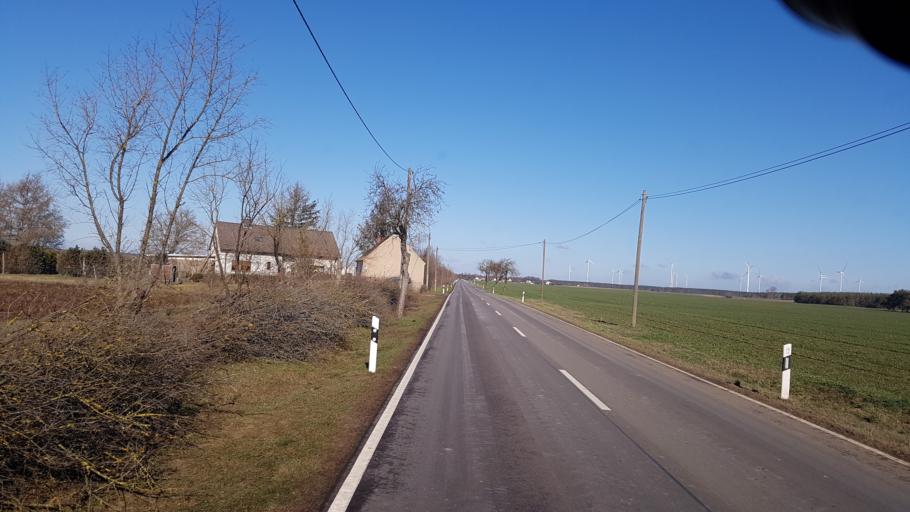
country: DE
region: Saxony
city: Arzberg
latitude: 51.5255
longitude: 13.1807
